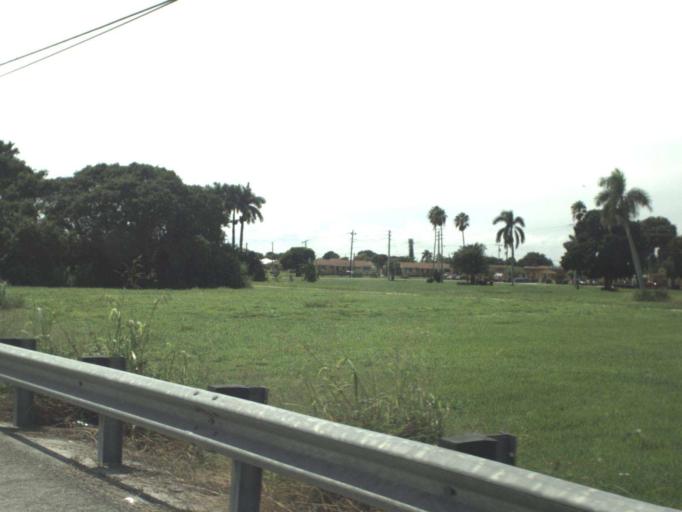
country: US
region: Florida
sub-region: Palm Beach County
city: Pahokee
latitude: 26.8148
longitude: -80.6657
